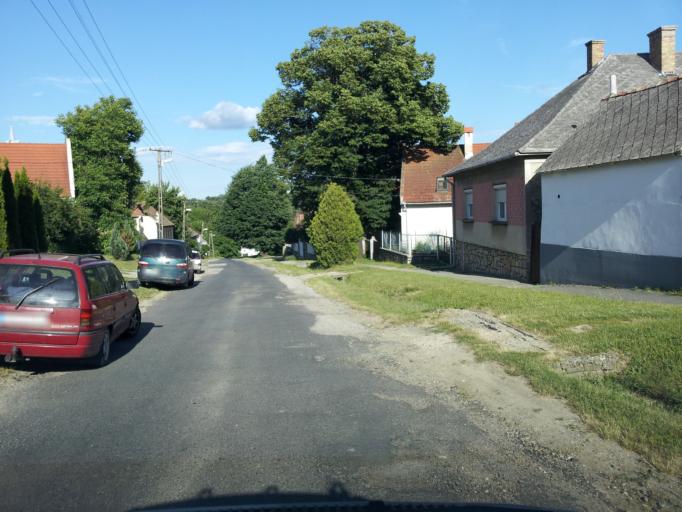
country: HU
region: Veszprem
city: Zirc
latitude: 47.2061
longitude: 17.8664
